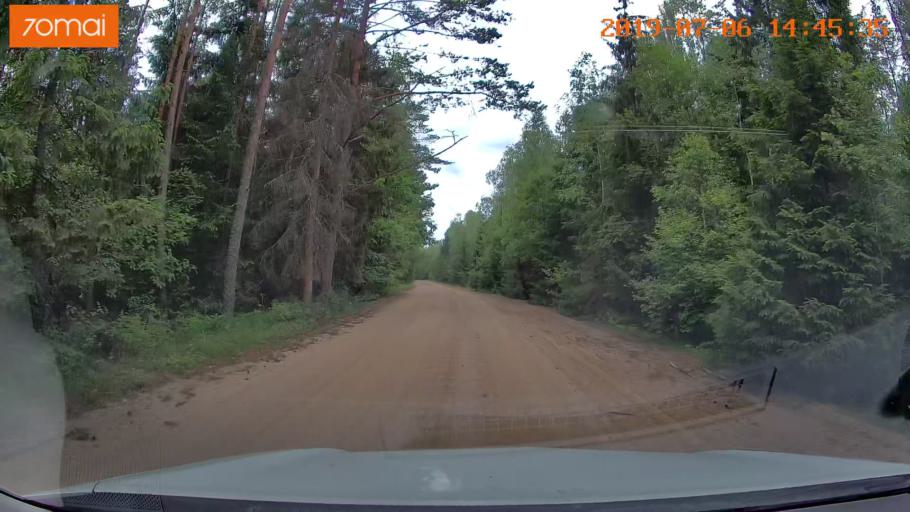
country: BY
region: Minsk
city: Ivyanyets
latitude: 53.9734
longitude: 26.6859
